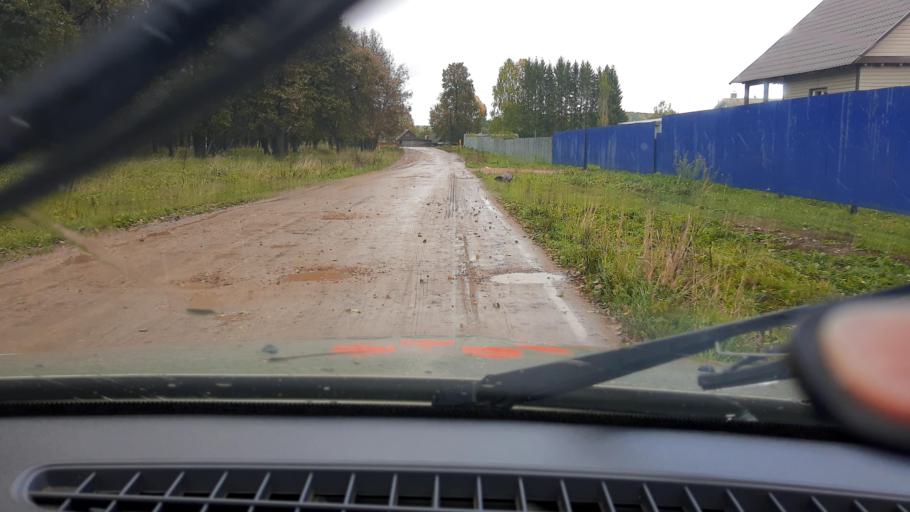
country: RU
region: Bashkortostan
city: Kudeyevskiy
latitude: 54.8797
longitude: 56.6320
